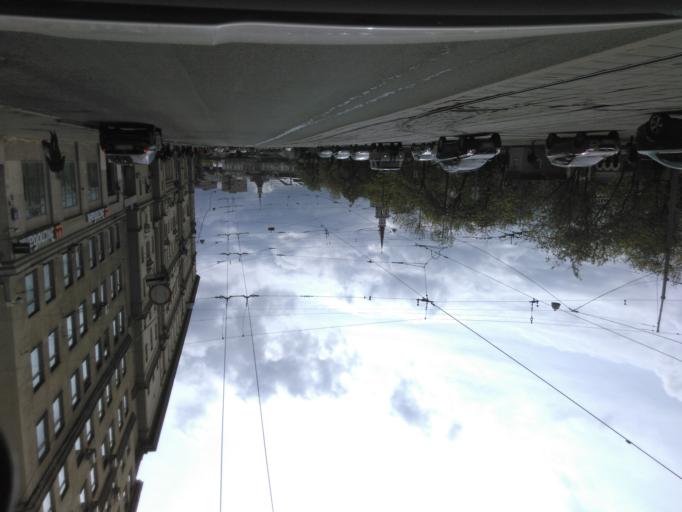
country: RU
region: Moscow
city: Sokol'niki
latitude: 55.7761
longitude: 37.6497
